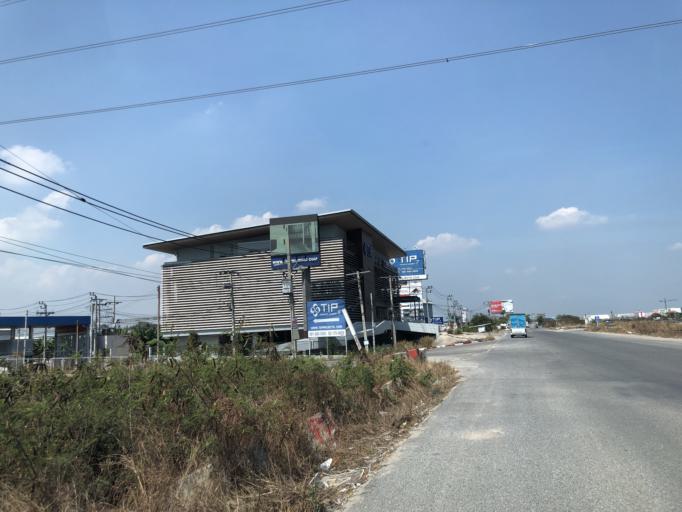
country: TH
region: Samut Prakan
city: Bang Bo District
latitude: 13.5808
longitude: 100.7578
